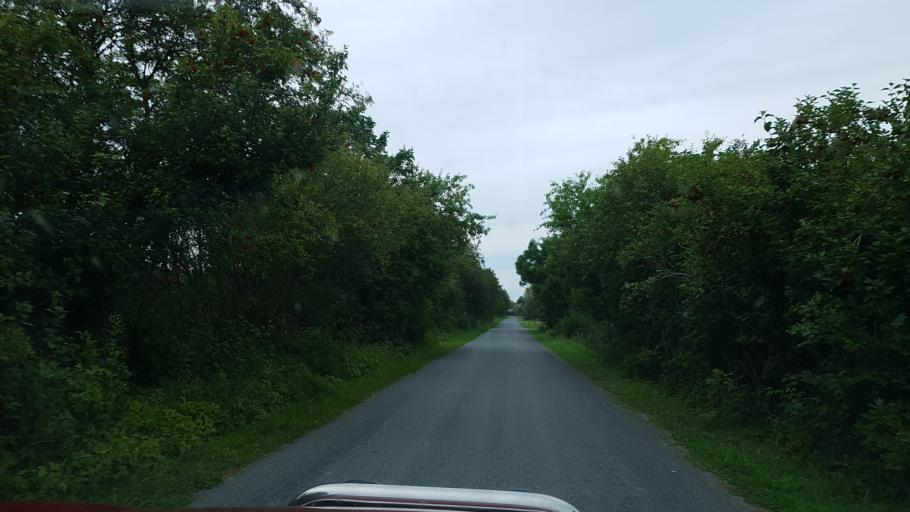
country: EE
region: Laeaene
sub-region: Ridala Parish
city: Uuemoisa
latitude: 58.7939
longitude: 23.6614
